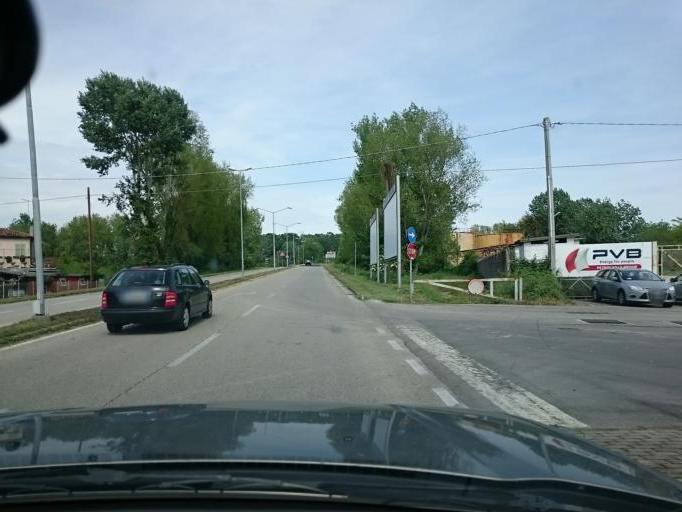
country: IT
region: Veneto
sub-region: Provincia di Padova
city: Padova
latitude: 45.4201
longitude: 11.8985
